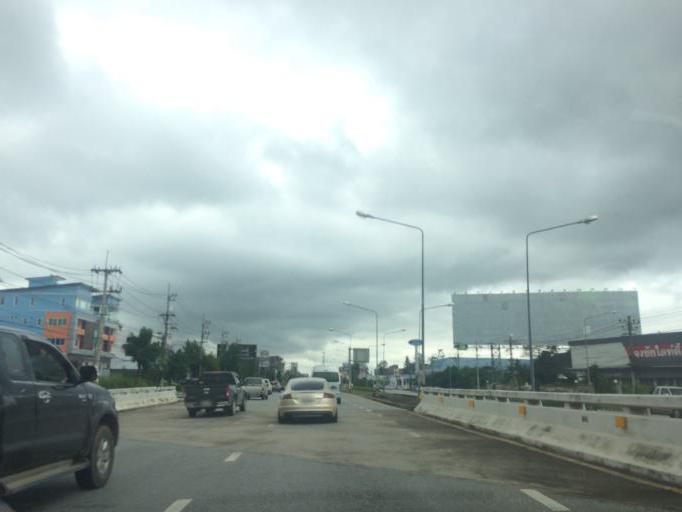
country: TH
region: Chiang Rai
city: Chiang Rai
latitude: 19.8800
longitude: 99.8333
